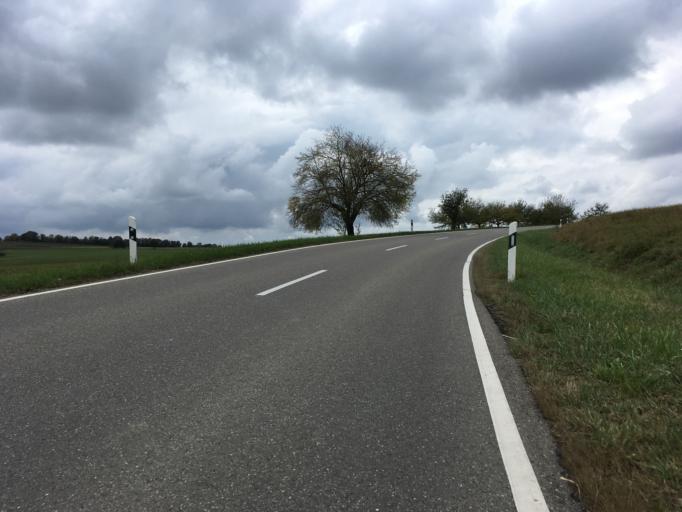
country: DE
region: Baden-Wuerttemberg
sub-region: Tuebingen Region
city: Gomaringen
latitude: 48.4717
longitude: 9.0939
